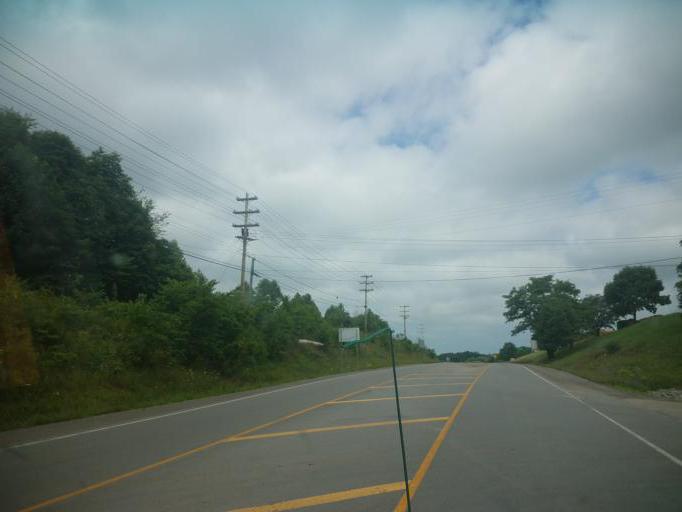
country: US
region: Kentucky
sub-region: Metcalfe County
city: Edmonton
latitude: 36.8776
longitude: -85.6660
